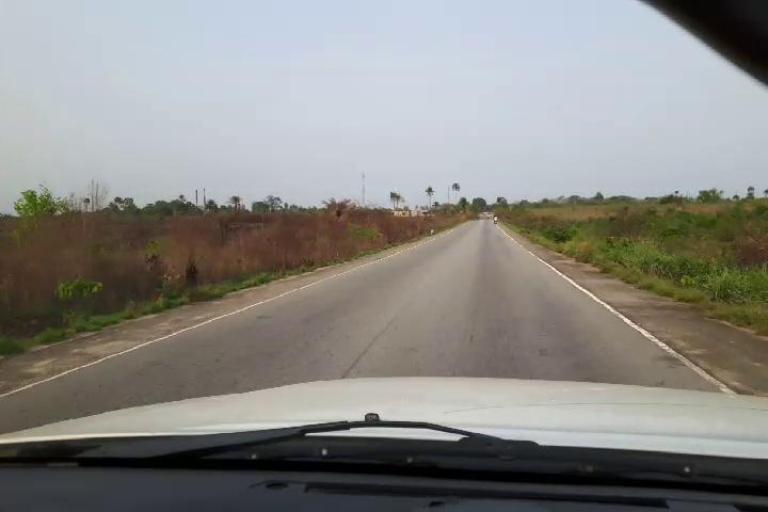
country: SL
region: Southern Province
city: Baoma
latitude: 7.9281
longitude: -11.5820
